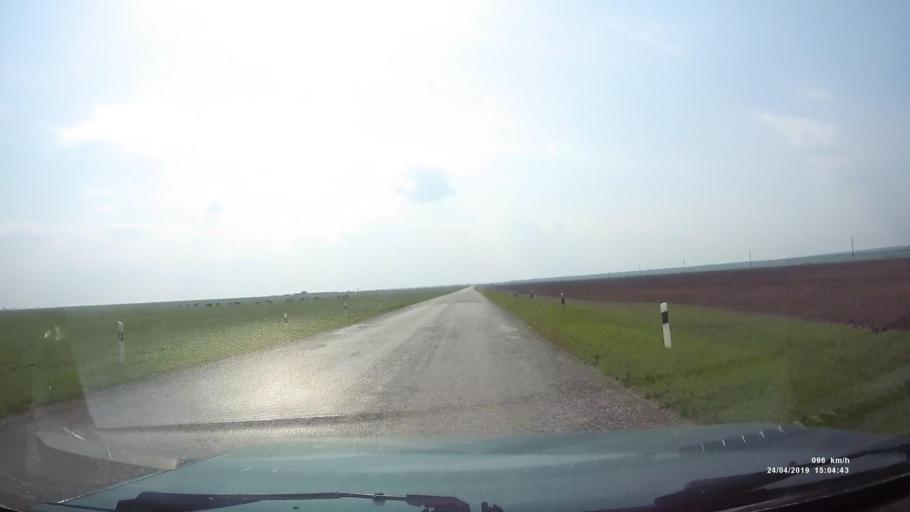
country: RU
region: Rostov
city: Remontnoye
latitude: 46.5615
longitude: 43.4646
